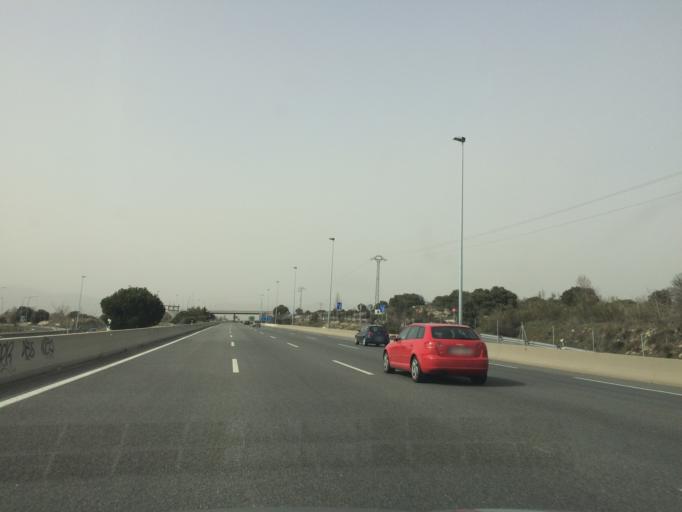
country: ES
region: Madrid
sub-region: Provincia de Madrid
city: Collado-Villalba
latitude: 40.6193
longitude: -3.9850
